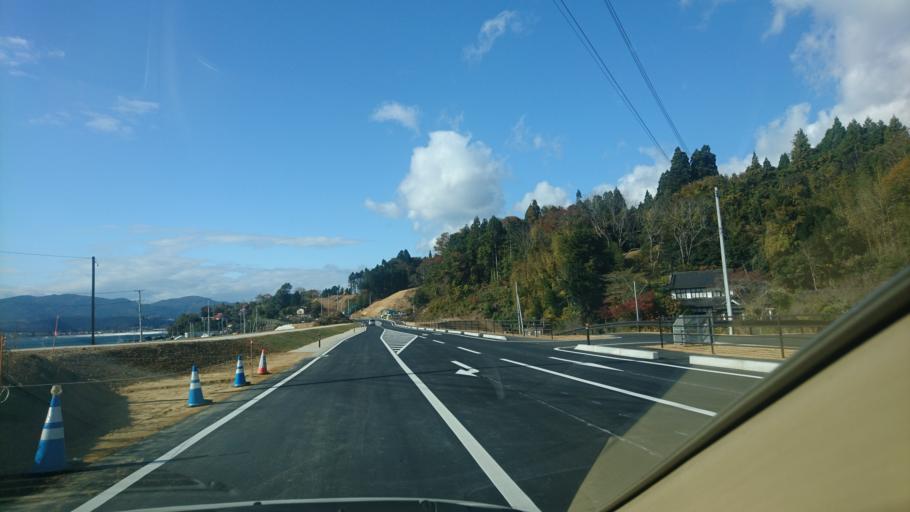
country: JP
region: Iwate
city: Ofunato
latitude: 38.8656
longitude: 141.6142
